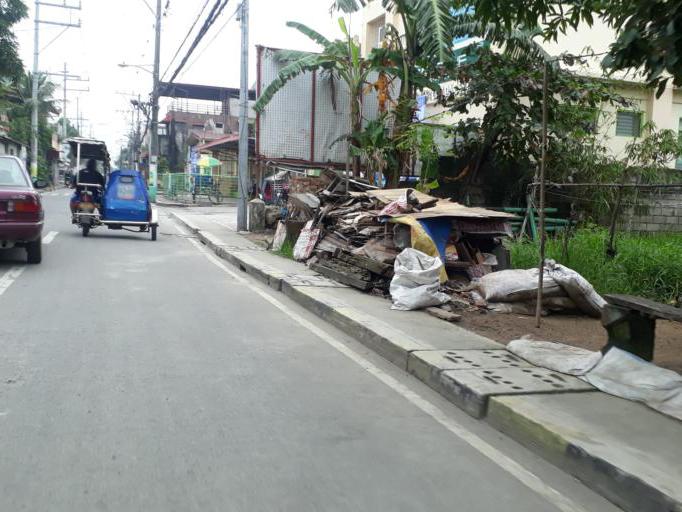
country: PH
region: Calabarzon
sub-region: Province of Rizal
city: Valenzuela
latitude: 14.7052
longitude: 120.9541
